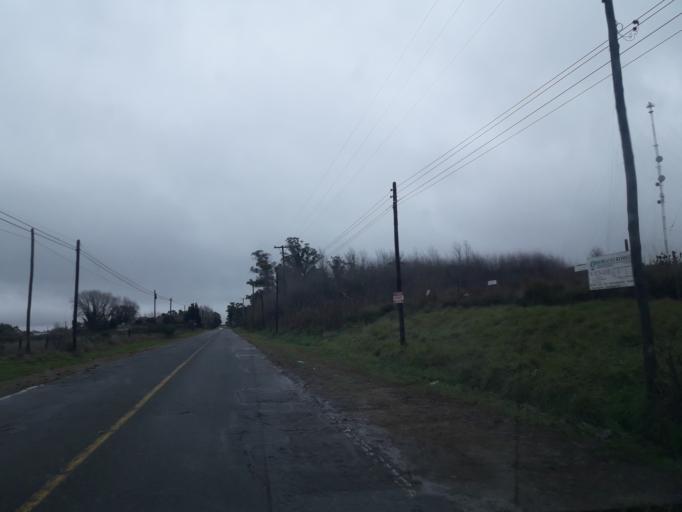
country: AR
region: Buenos Aires
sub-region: Partido de Tandil
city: Tandil
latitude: -37.3256
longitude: -59.1721
